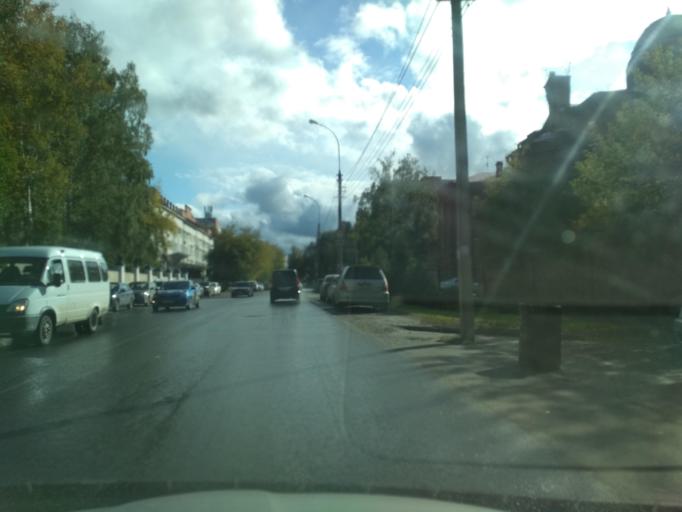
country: RU
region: Tomsk
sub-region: Tomskiy Rayon
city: Tomsk
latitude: 56.4657
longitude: 84.9757
